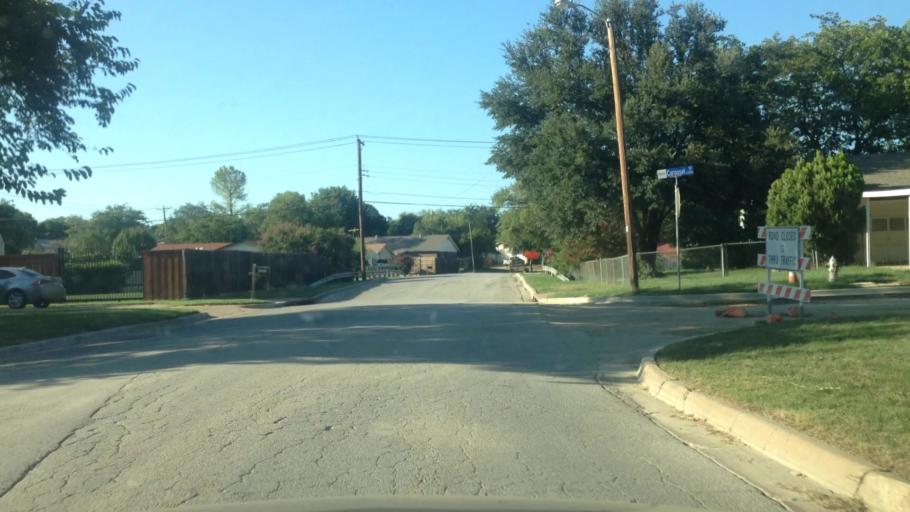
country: US
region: Texas
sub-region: Tarrant County
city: Watauga
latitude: 32.8621
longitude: -97.2463
